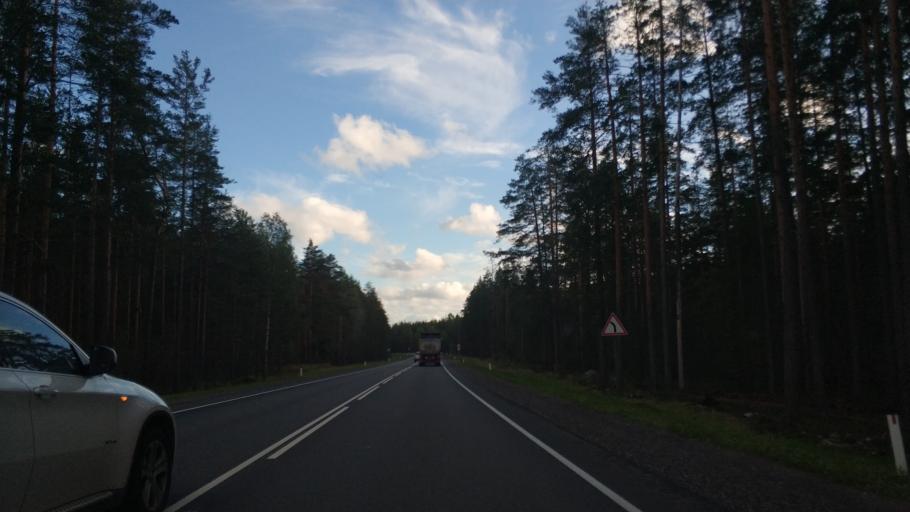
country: RU
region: Leningrad
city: Priozersk
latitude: 60.8840
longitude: 30.1608
